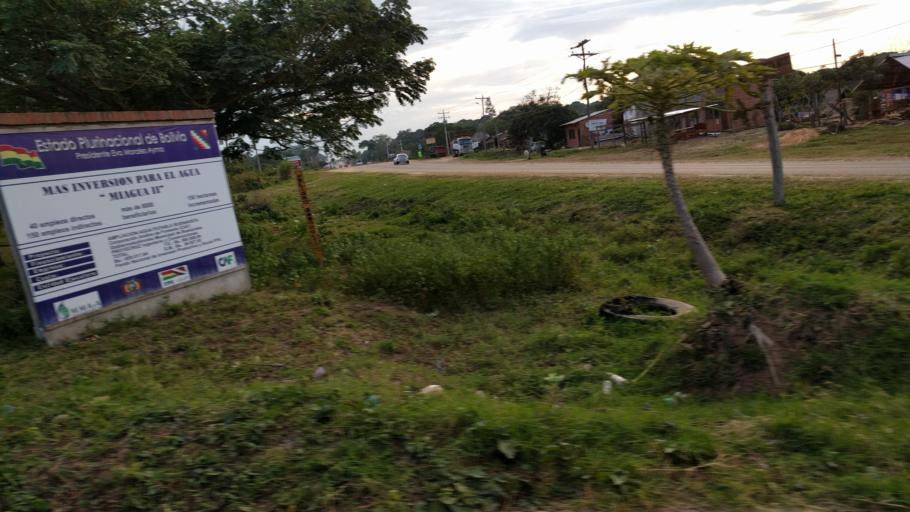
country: BO
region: Santa Cruz
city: Buena Vista
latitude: -17.4550
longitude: -63.6569
